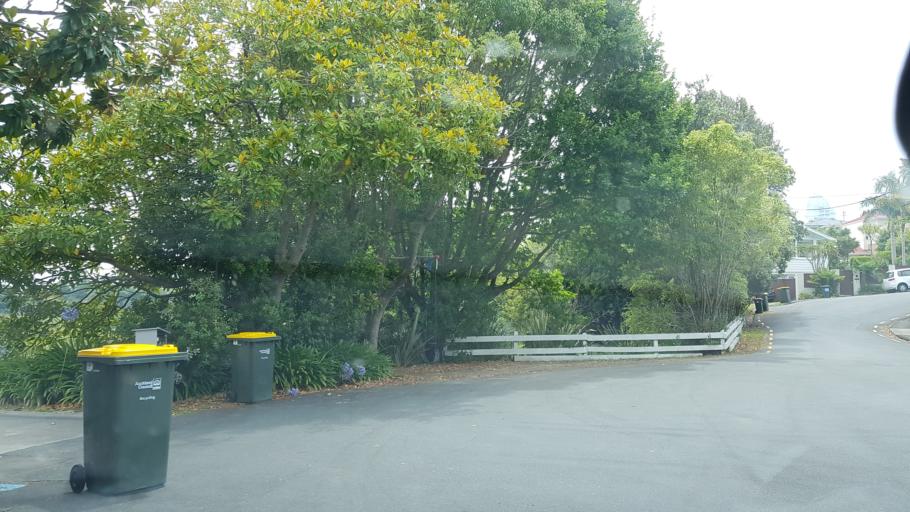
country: NZ
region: Auckland
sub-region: Auckland
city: North Shore
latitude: -36.7974
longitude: 174.7732
